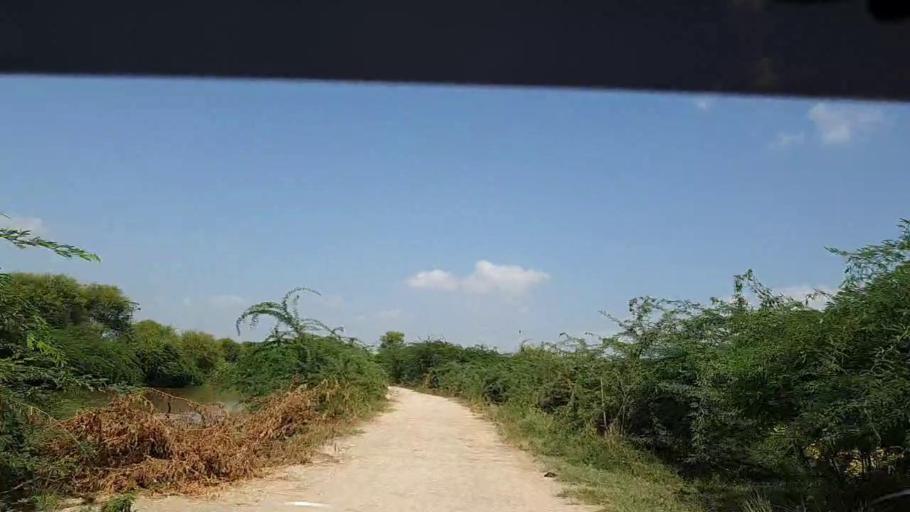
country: PK
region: Sindh
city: Badin
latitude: 24.5916
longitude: 68.7971
